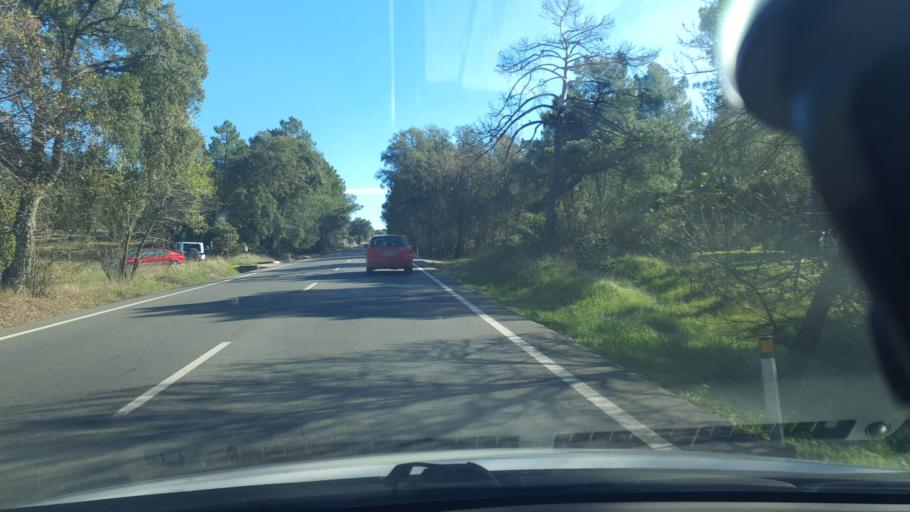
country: ES
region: Castille and Leon
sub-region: Provincia de Avila
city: Piedralaves
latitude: 40.3137
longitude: -4.6676
